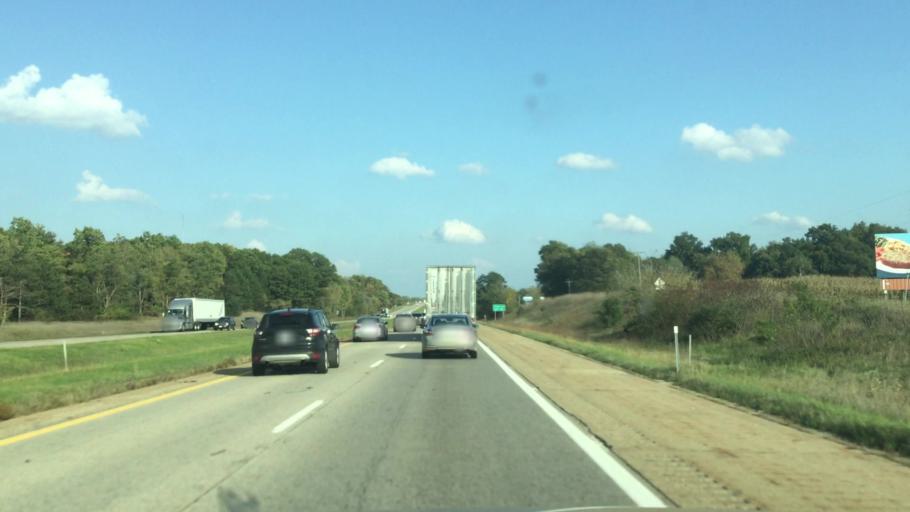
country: US
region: Michigan
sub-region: Jackson County
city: Concord
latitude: 42.2620
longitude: -84.6628
